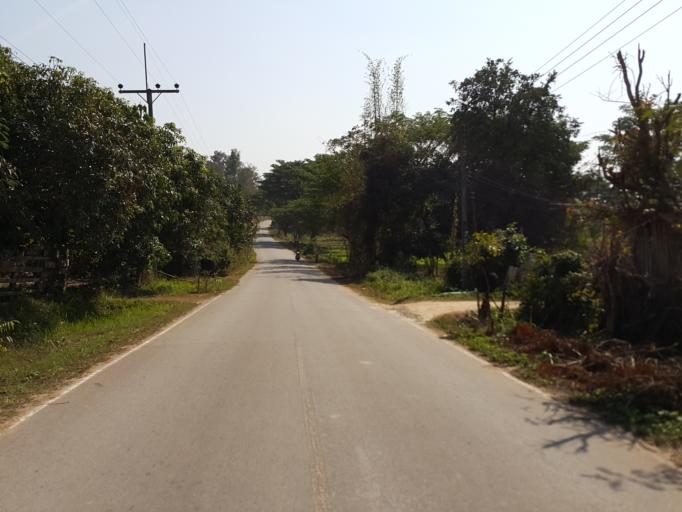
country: TH
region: Lampang
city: Wang Nuea
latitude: 19.0445
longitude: 99.6240
